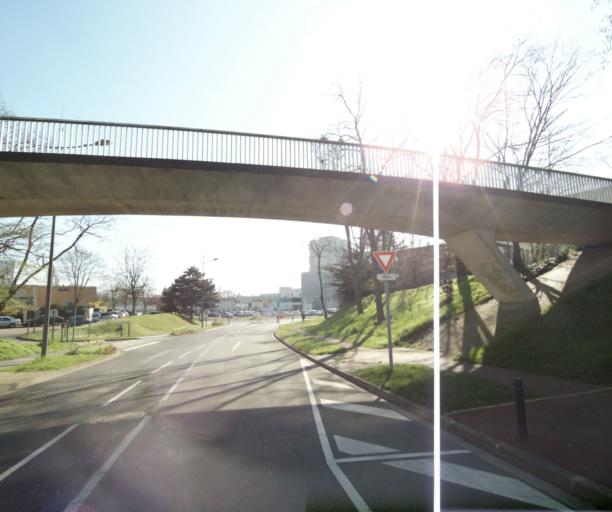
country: FR
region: Ile-de-France
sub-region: Departement du Val-d'Oise
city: Cergy
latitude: 49.0317
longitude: 2.0840
